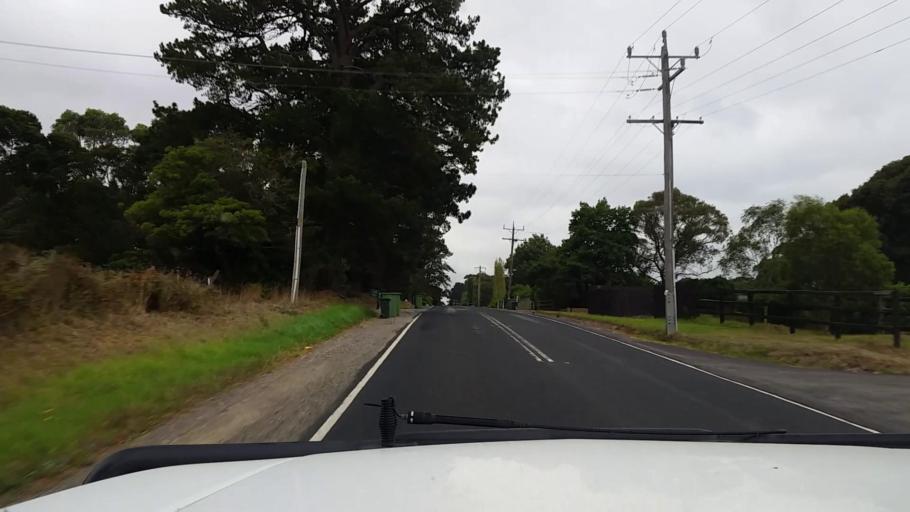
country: AU
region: Victoria
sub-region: Mornington Peninsula
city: Hastings
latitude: -38.2915
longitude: 145.1456
